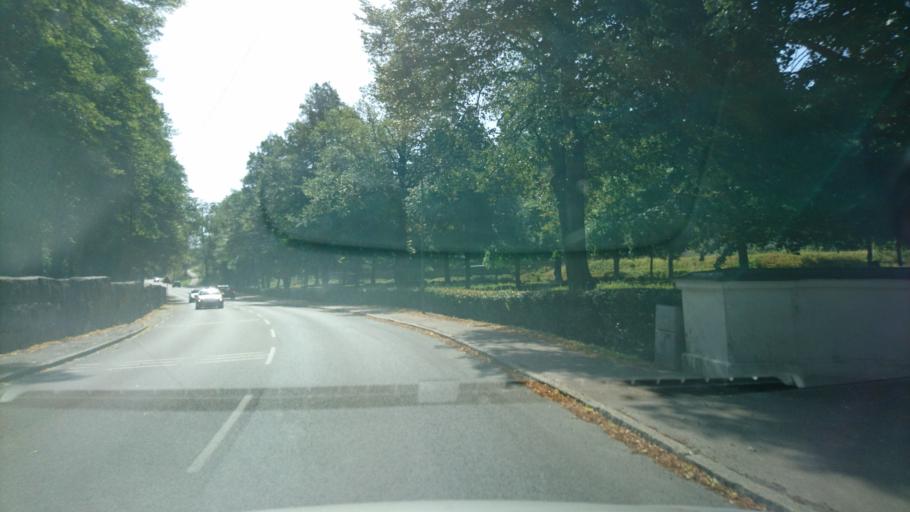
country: SE
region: Soedermanland
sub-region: Strangnas Kommun
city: Strangnas
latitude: 59.3701
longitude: 17.0333
